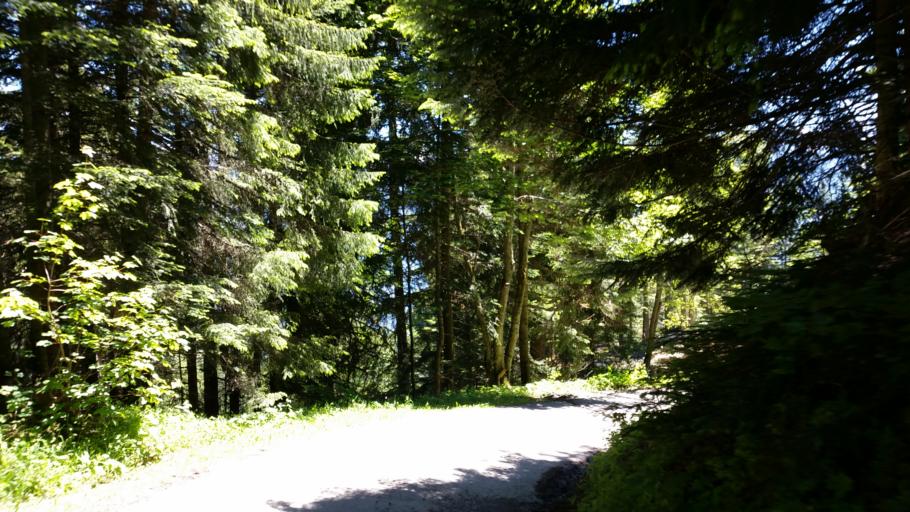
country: CH
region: Valais
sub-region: Martigny District
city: Saillon
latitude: 46.2081
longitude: 7.1765
